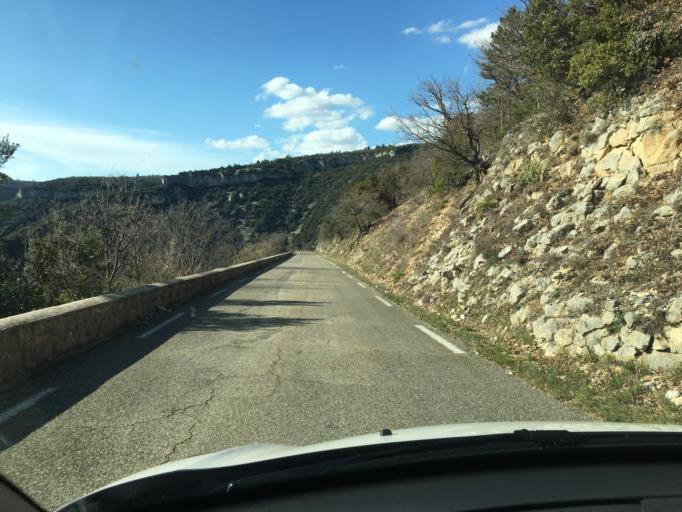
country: FR
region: Provence-Alpes-Cote d'Azur
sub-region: Departement du Vaucluse
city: Villes-sur-Auzon
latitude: 44.0611
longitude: 5.3209
